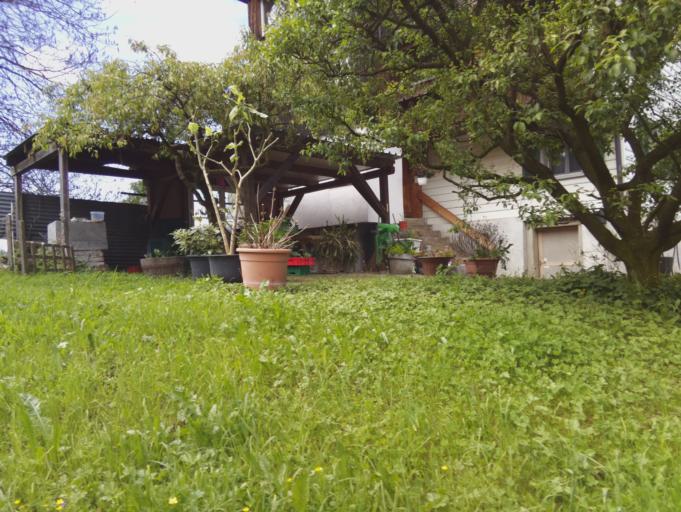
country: CH
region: Schwyz
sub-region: Bezirk March
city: Schubelbach
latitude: 47.1723
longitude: 8.9265
